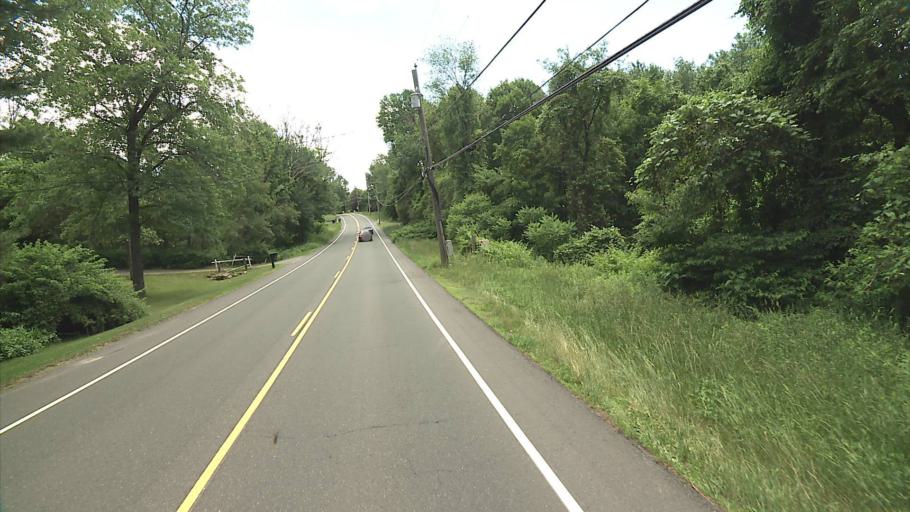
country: US
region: Connecticut
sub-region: Litchfield County
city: Watertown
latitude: 41.6484
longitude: -73.1505
